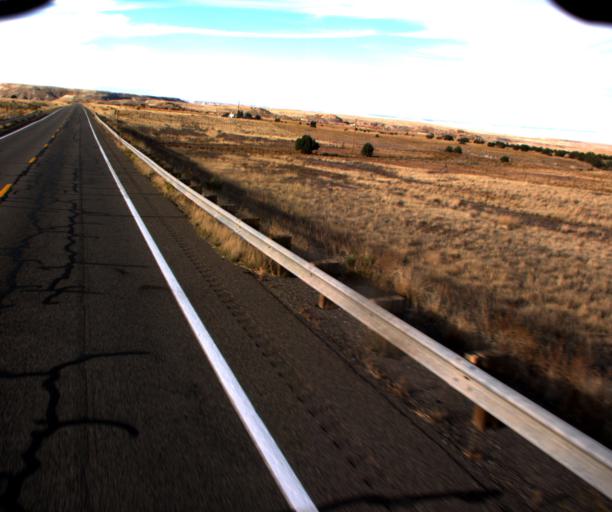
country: US
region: New Mexico
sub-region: San Juan County
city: Shiprock
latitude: 36.9041
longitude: -109.0690
